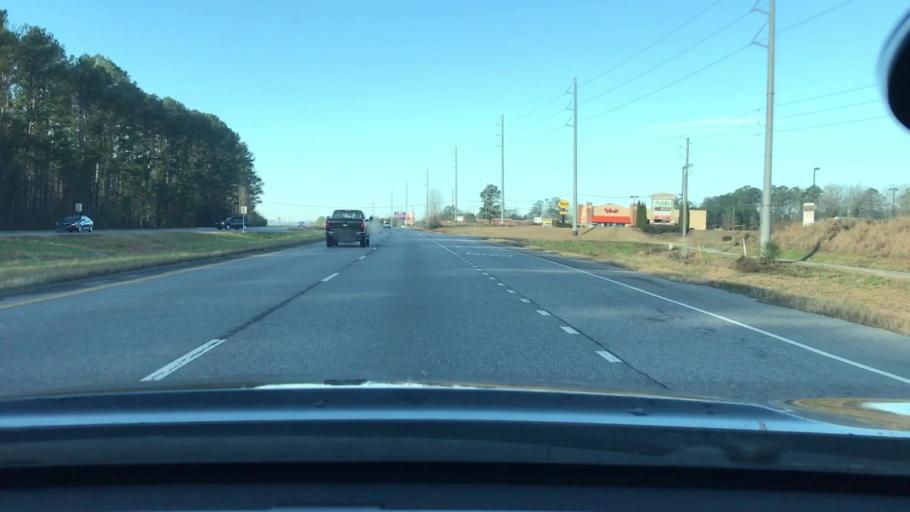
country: US
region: Alabama
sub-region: Shelby County
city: Chelsea
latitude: 33.3512
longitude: -86.6070
